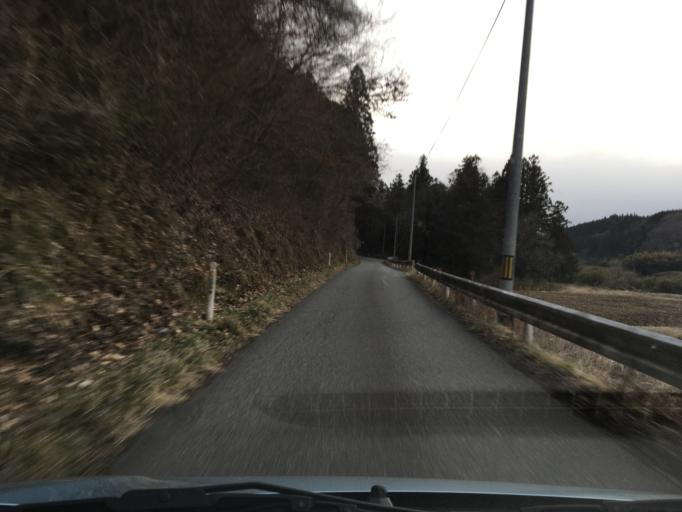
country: JP
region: Iwate
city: Ichinoseki
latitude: 38.8674
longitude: 141.2650
